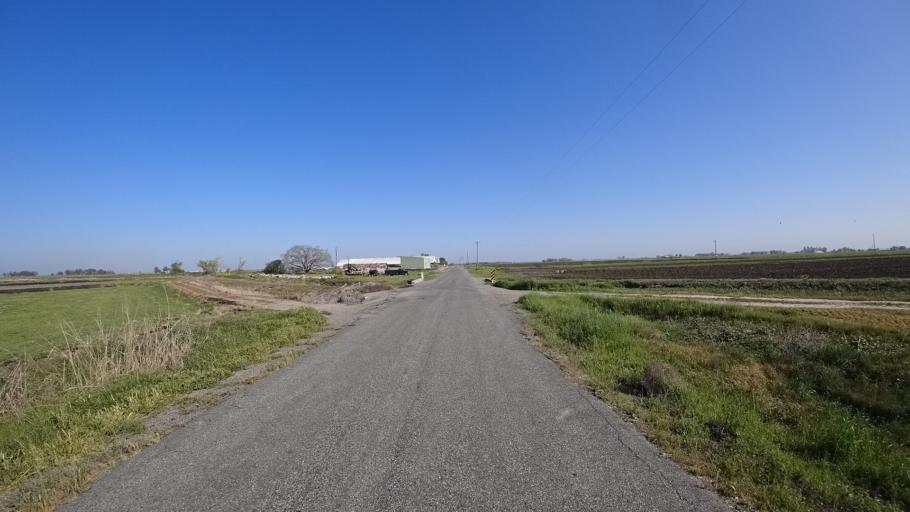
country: US
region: California
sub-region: Glenn County
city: Willows
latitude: 39.5713
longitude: -122.0839
